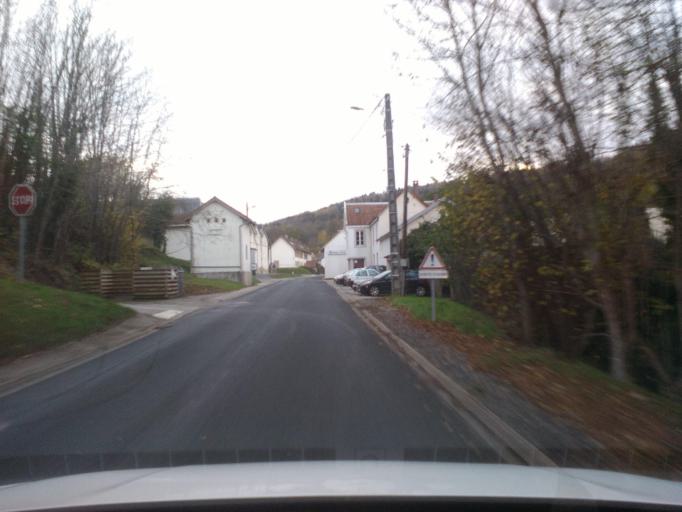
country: FR
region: Lorraine
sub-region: Departement des Vosges
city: Ban-de-Laveline
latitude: 48.2240
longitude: 7.0531
